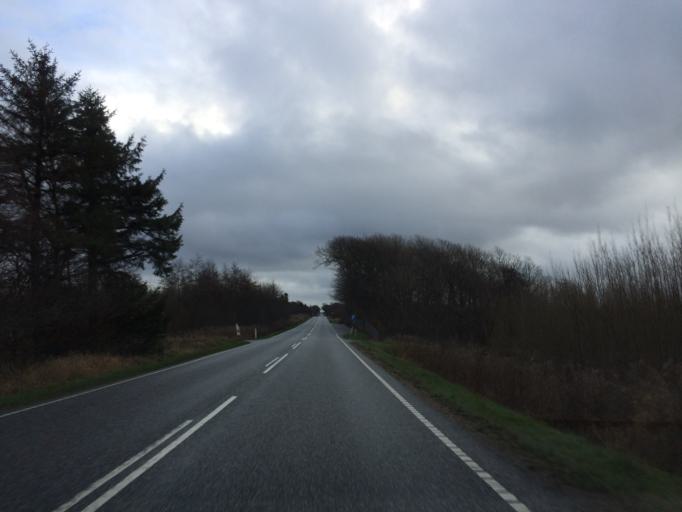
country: DK
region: Central Jutland
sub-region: Ringkobing-Skjern Kommune
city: Skjern
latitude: 56.0476
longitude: 8.3996
